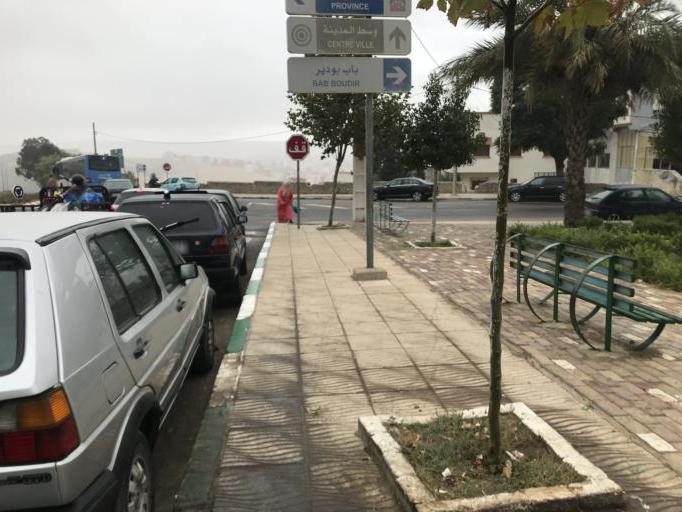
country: MA
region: Taza-Al Hoceima-Taounate
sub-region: Taza
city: Taza
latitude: 34.2039
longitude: -4.0162
